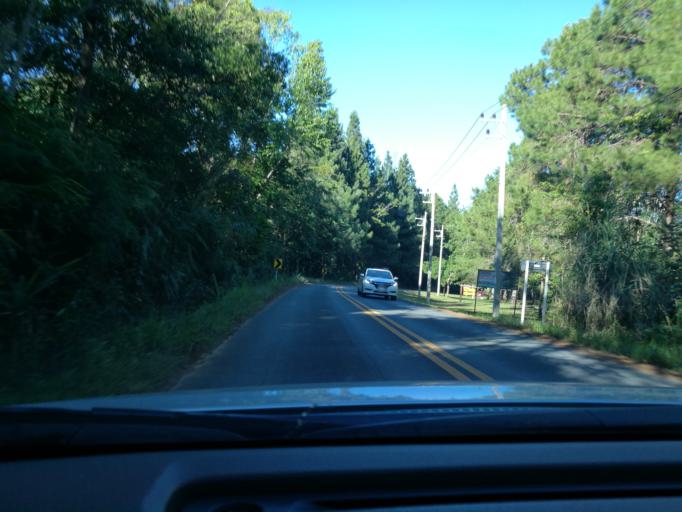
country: TH
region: Phitsanulok
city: Nakhon Thai
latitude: 16.9944
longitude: 101.0126
